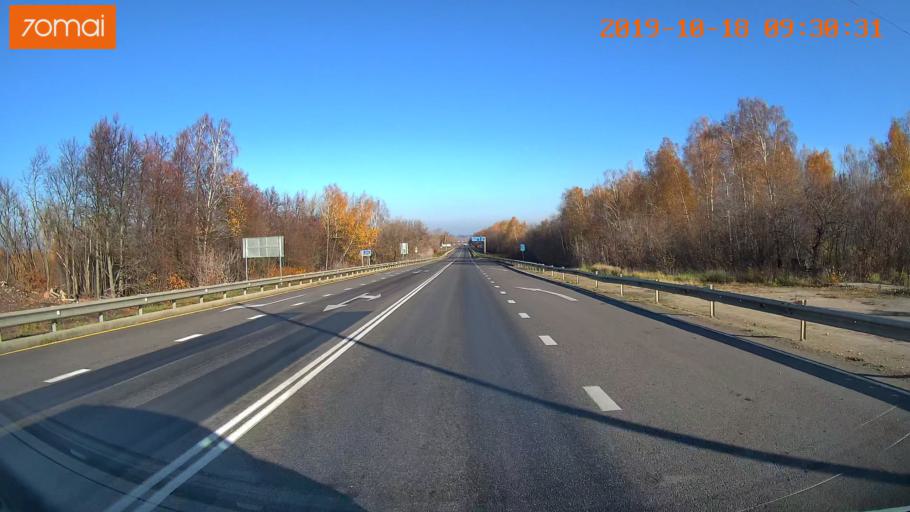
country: RU
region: Tula
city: Yefremov
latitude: 53.1396
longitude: 38.1596
